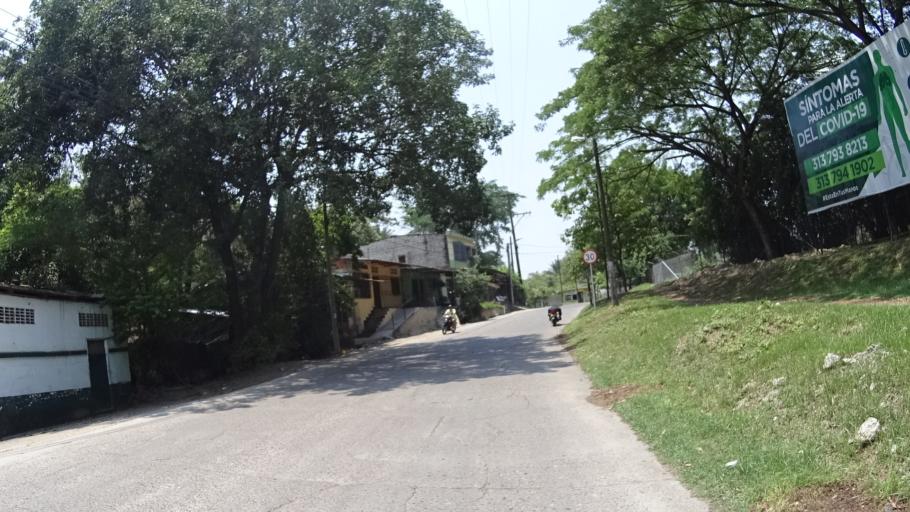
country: CO
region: Cundinamarca
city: Puerto Salgar
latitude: 5.4620
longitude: -74.6655
